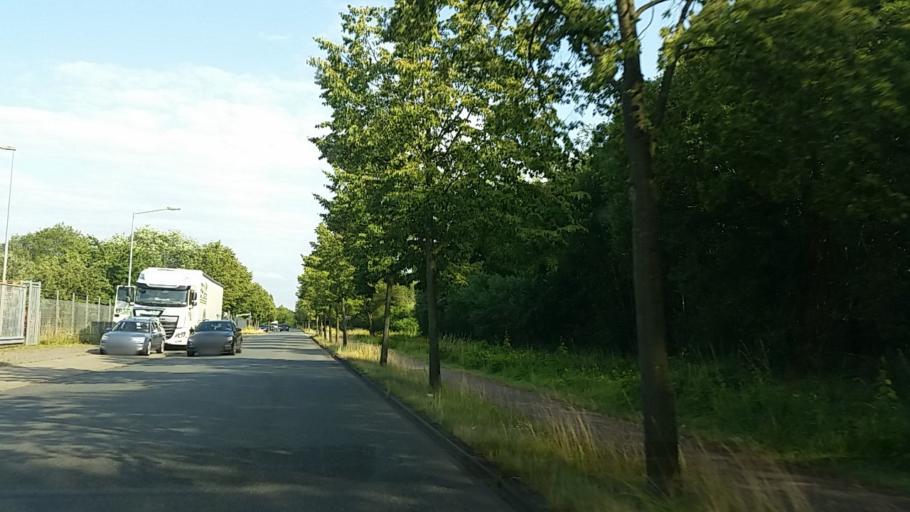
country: DE
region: Lower Saxony
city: Winsen
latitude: 53.3395
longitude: 10.2302
